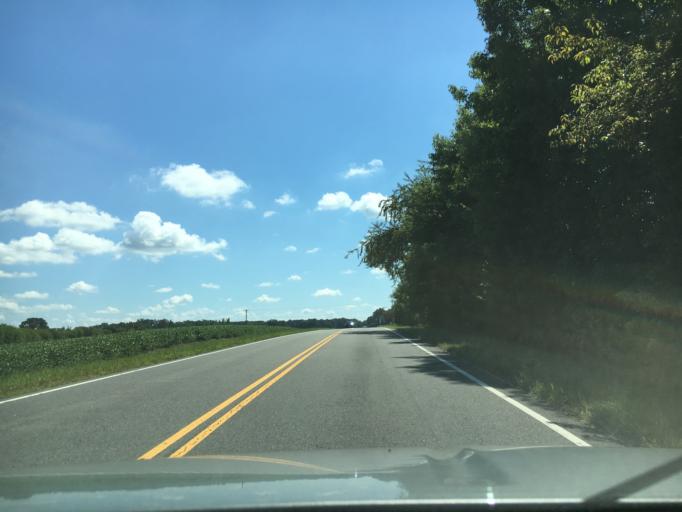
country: US
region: Virginia
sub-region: Amelia County
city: Amelia Court House
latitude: 37.3896
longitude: -77.8990
